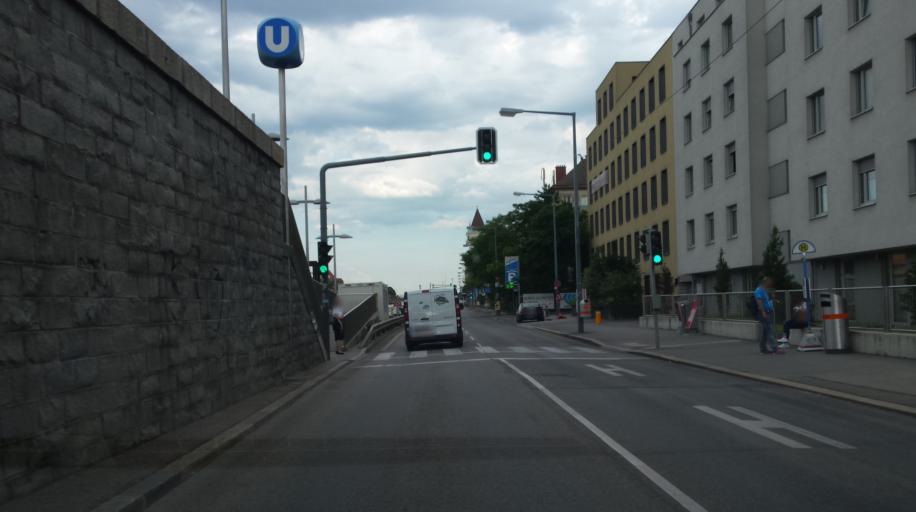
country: AT
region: Lower Austria
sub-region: Politischer Bezirk Modling
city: Perchtoldsdorf
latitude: 48.1891
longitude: 16.2967
